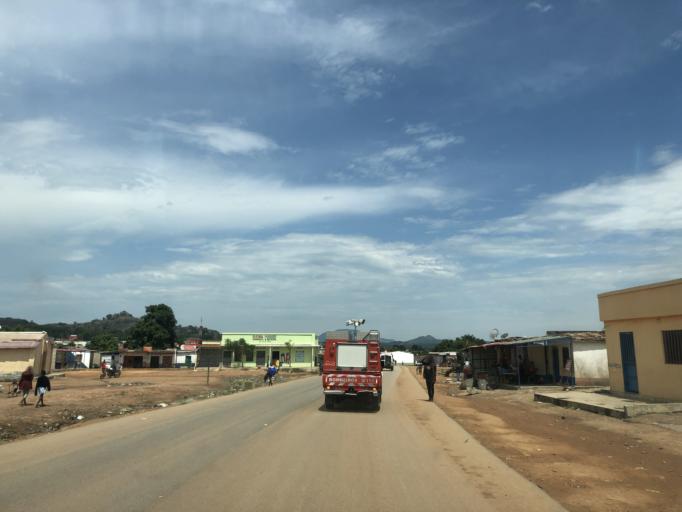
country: AO
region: Cuanza Sul
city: Quibala
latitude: -10.7362
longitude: 14.9882
